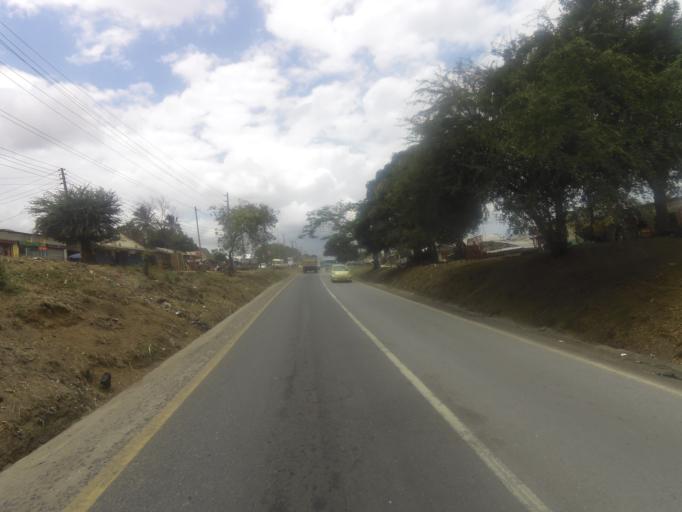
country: TZ
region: Pwani
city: Vikindu
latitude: -6.9409
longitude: 39.2782
